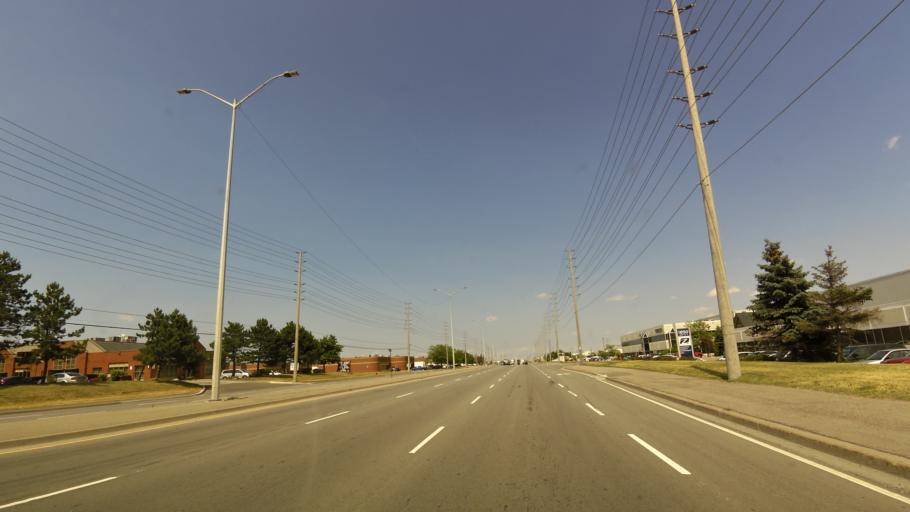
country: CA
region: Ontario
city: Brampton
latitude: 43.6816
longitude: -79.6668
